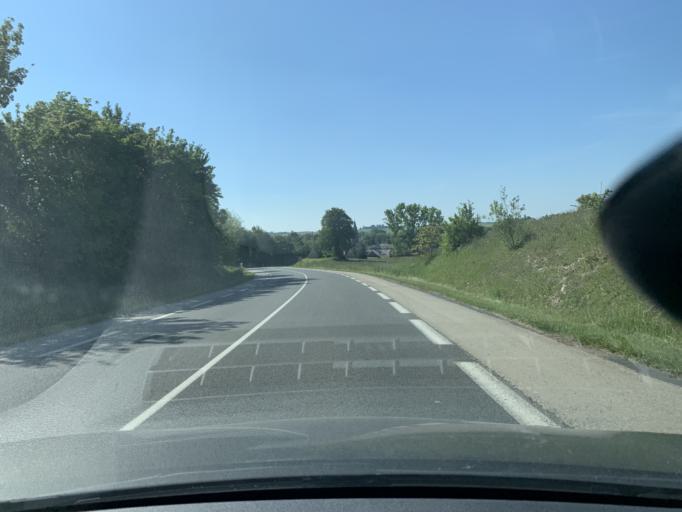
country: FR
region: Nord-Pas-de-Calais
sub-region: Departement du Nord
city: Rumilly-en-Cambresis
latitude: 50.1124
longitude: 3.2473
